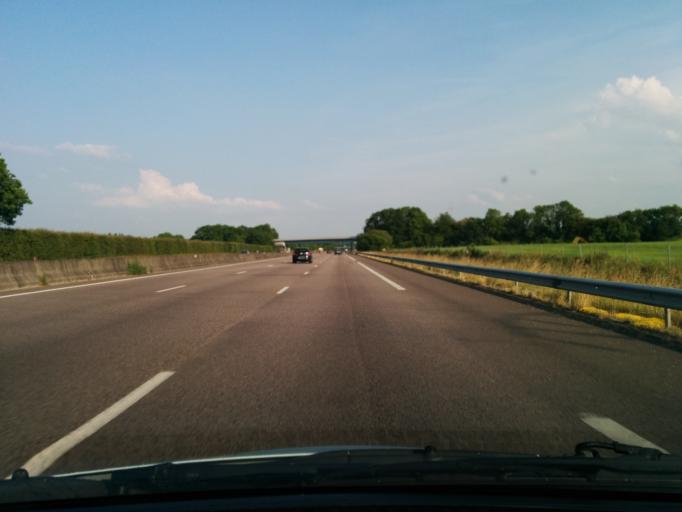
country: FR
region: Haute-Normandie
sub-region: Departement de l'Eure
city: La Chapelle-Reanville
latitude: 49.0954
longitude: 1.3610
